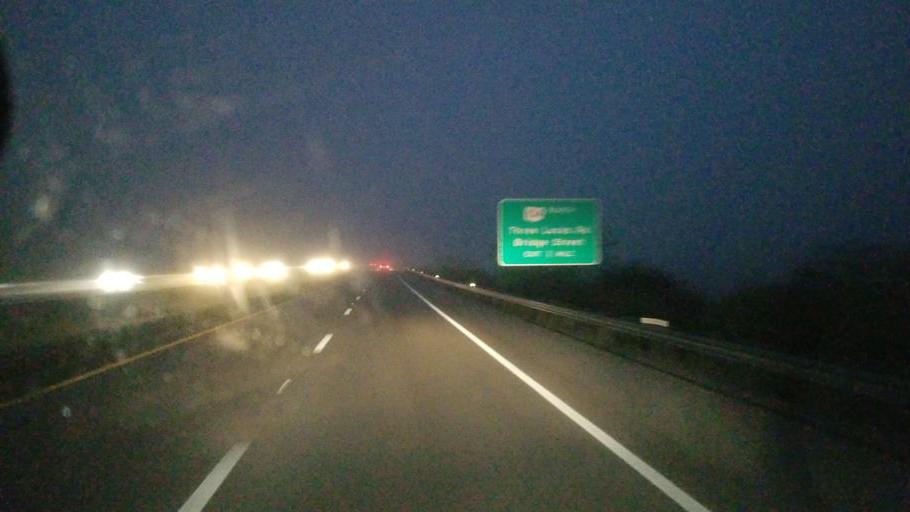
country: US
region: Ohio
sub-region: Ross County
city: Chillicothe
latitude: 39.3065
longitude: -82.9412
